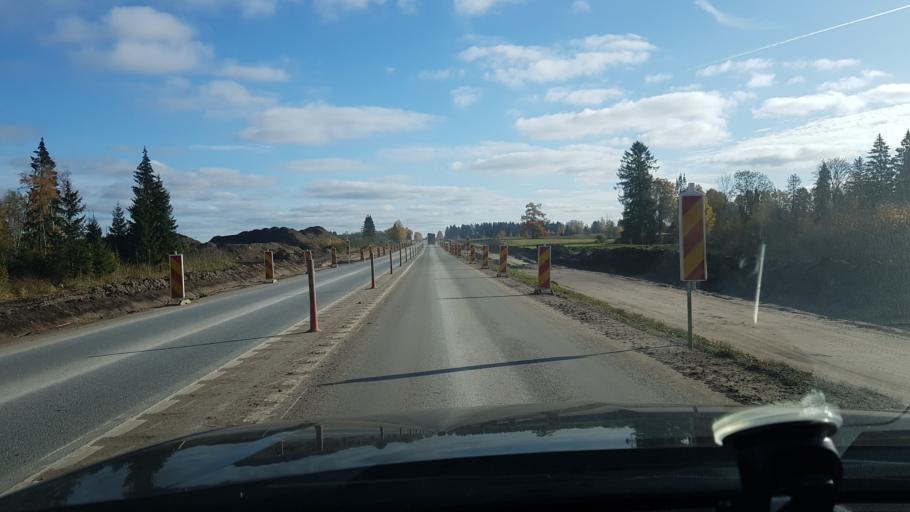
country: EE
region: Laeaene-Virumaa
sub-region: Kadrina vald
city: Kadrina
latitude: 59.4373
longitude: 26.1492
